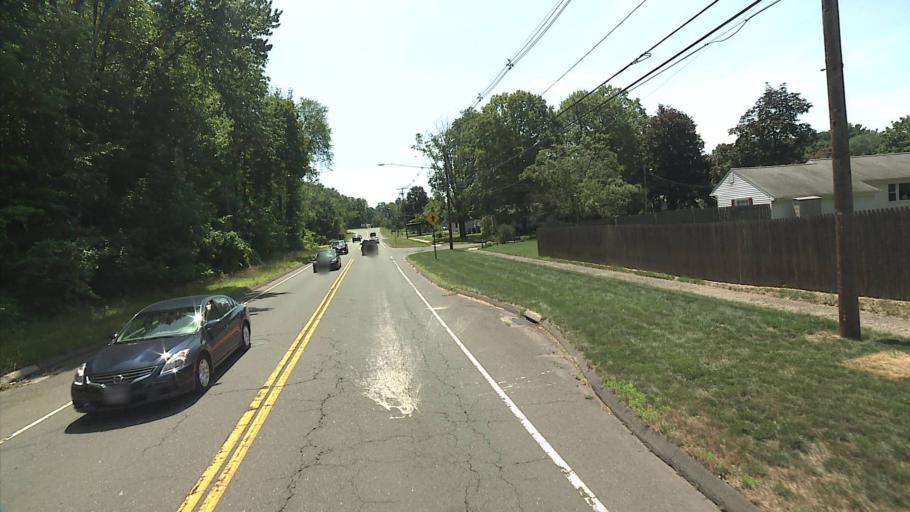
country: US
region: Connecticut
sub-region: Hartford County
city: New Britain
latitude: 41.6497
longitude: -72.7930
